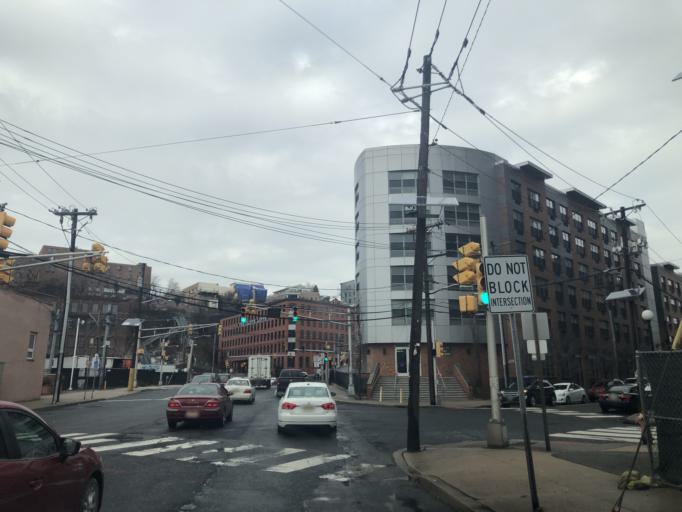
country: US
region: New Jersey
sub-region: Hudson County
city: Hoboken
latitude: 40.7393
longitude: -74.0428
